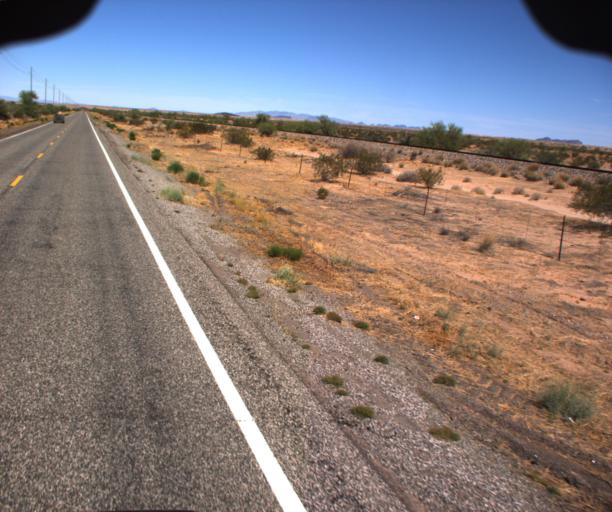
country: US
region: Arizona
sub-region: La Paz County
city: Cienega Springs
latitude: 33.9809
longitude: -114.0593
